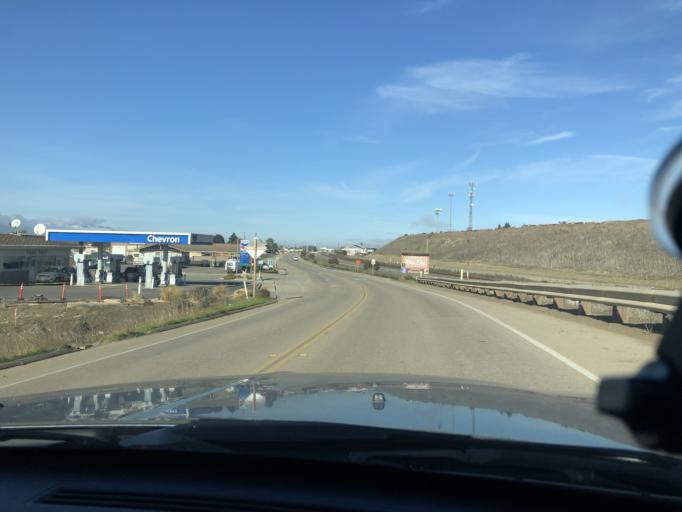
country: US
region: California
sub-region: Monterey County
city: King City
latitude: 36.2026
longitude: -121.1130
